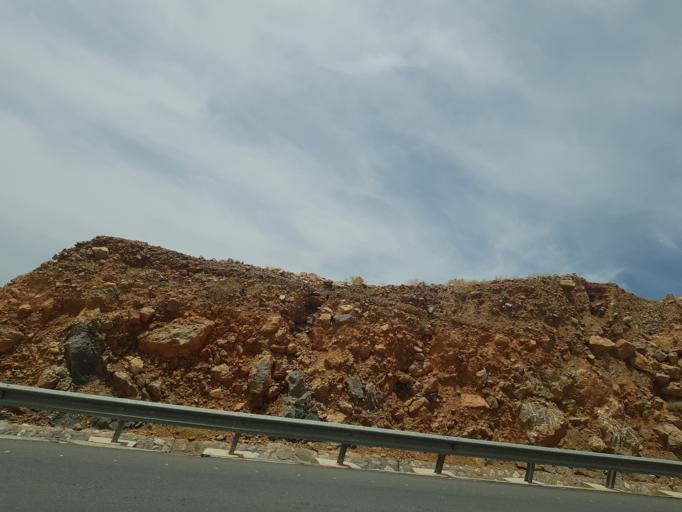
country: OM
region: Muhafazat ad Dakhiliyah
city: Izki
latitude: 22.9803
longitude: 57.7018
